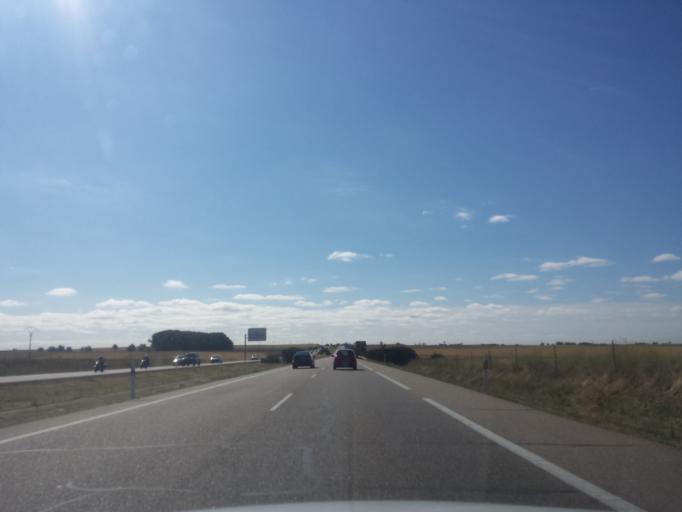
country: ES
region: Castille and Leon
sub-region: Provincia de Zamora
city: San Esteban del Molar
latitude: 41.9573
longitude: -5.5777
